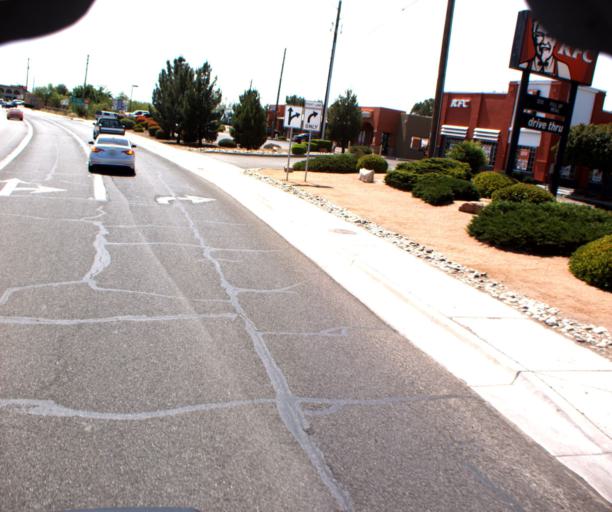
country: US
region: Arizona
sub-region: Yavapai County
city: Verde Village
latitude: 34.7226
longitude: -112.0045
